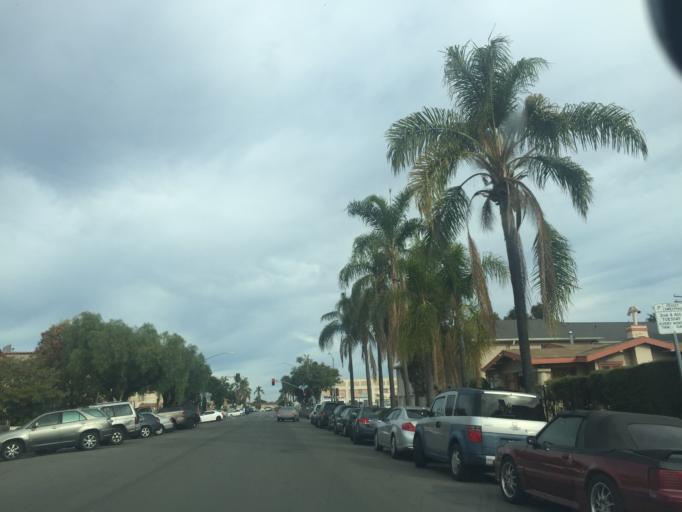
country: US
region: California
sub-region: San Diego County
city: San Diego
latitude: 32.7486
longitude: -117.1032
